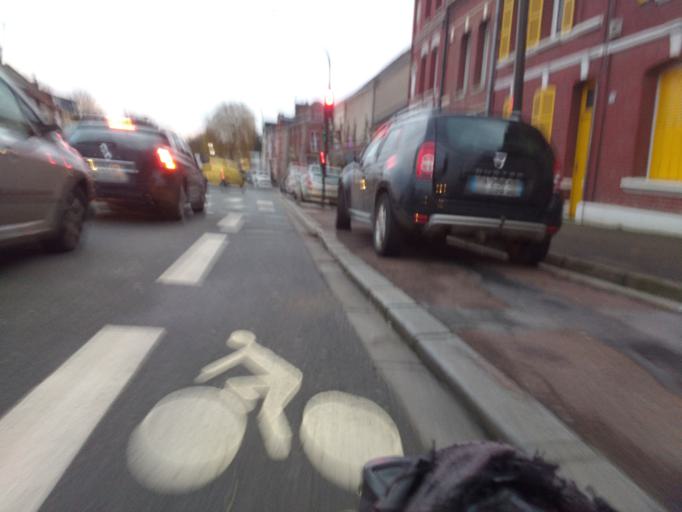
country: FR
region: Picardie
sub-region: Departement de la Somme
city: Camon
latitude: 49.8794
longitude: 2.3345
